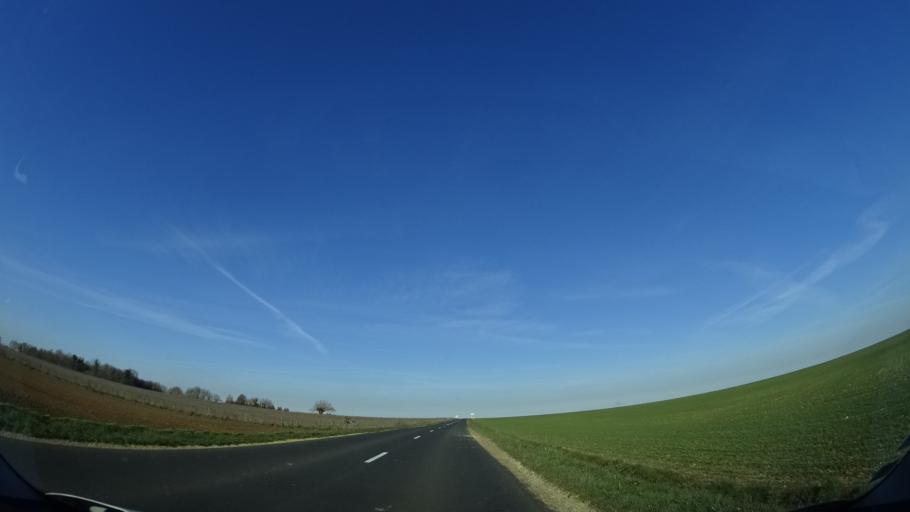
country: FR
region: Poitou-Charentes
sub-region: Departement de la Vienne
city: Saint-Jean-de-Sauves
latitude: 46.7976
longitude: 0.1053
